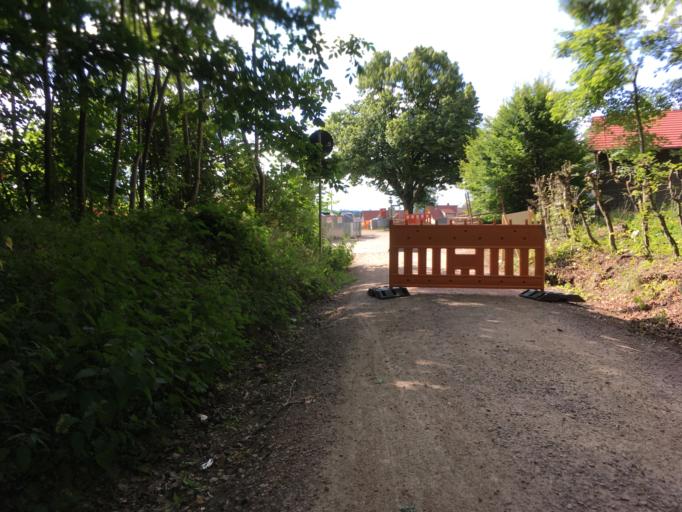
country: DE
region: Baden-Wuerttemberg
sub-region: Karlsruhe Region
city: Lossburg
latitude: 48.4237
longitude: 8.4408
